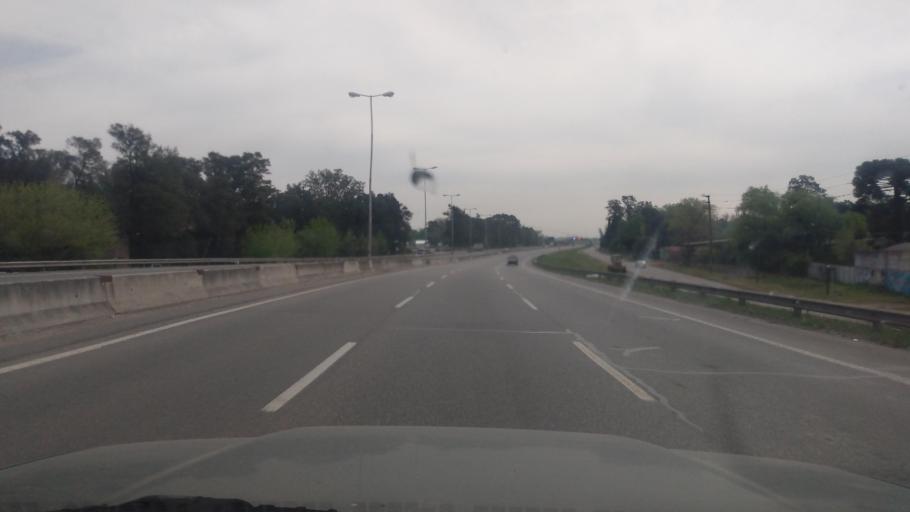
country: AR
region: Buenos Aires
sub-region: Partido de Pilar
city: Pilar
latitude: -34.4298
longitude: -58.9942
